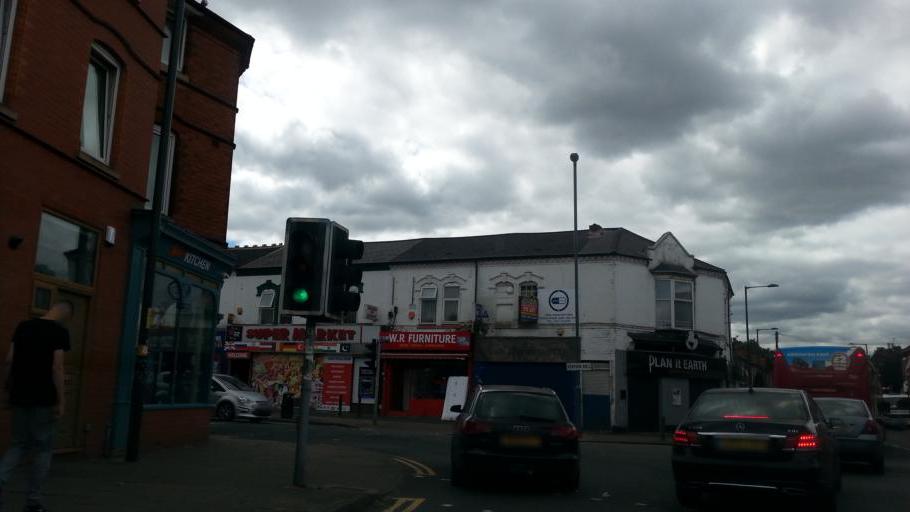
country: GB
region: England
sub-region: City and Borough of Birmingham
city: Sutton Coldfield
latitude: 52.5284
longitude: -1.8414
